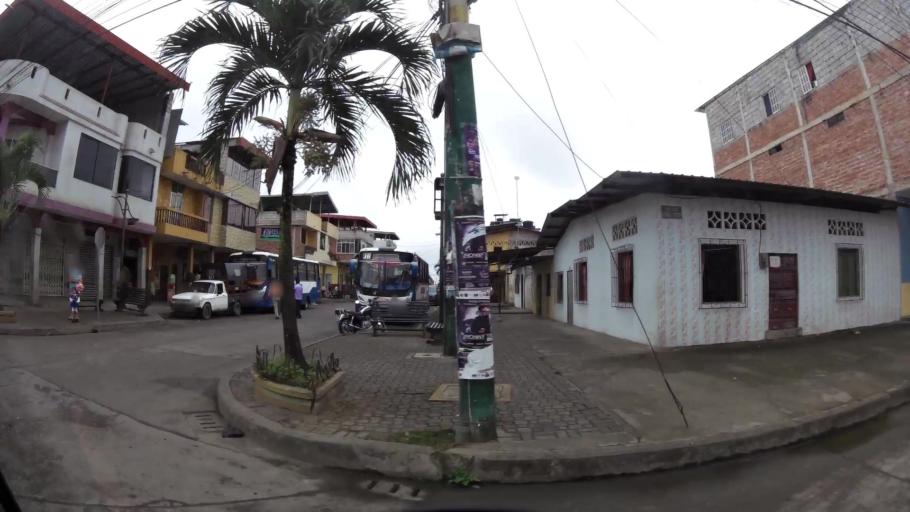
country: EC
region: El Oro
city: Pasaje
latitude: -3.3257
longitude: -79.8116
